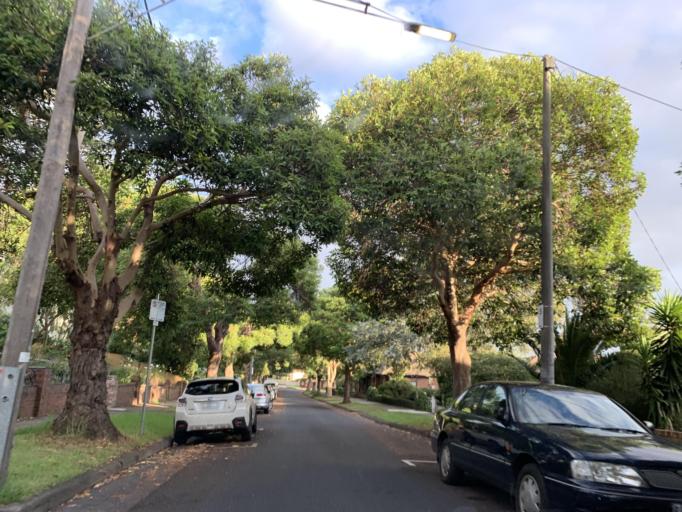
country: AU
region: Victoria
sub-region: Moonee Valley
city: Travancore
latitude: -37.7789
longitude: 144.9347
